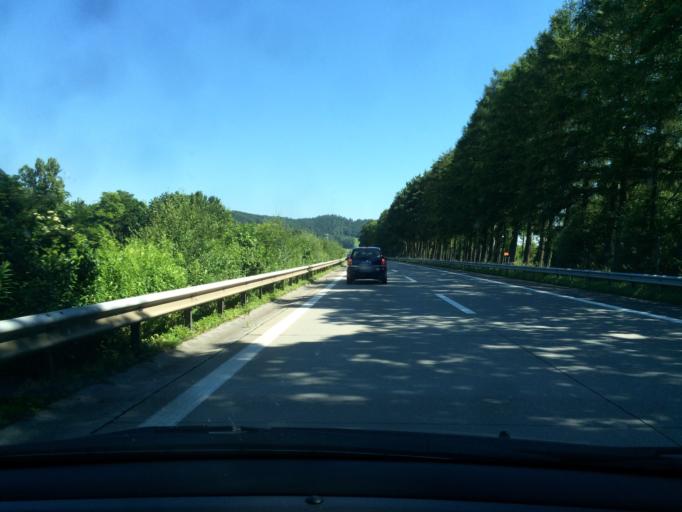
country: CH
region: Saint Gallen
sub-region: Wahlkreis Rheintal
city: Ruthi
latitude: 47.2898
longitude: 9.5510
